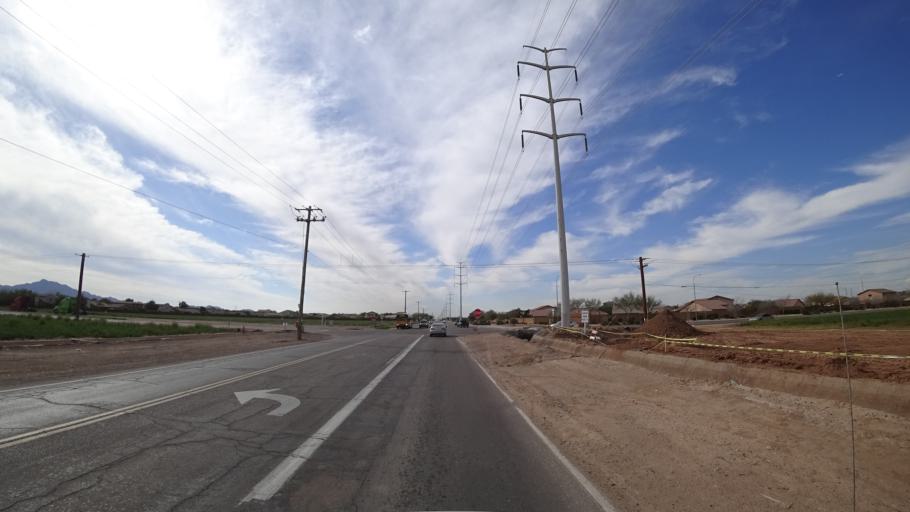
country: US
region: Arizona
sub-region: Maricopa County
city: Tolleson
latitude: 33.4065
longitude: -112.2716
